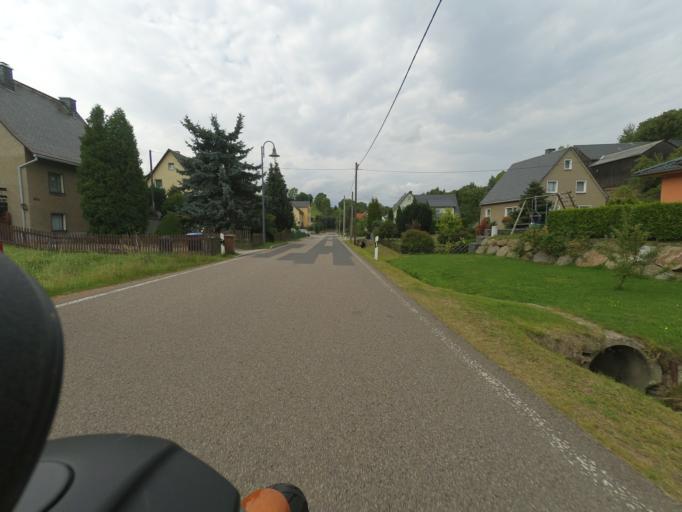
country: DE
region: Saxony
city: Glashutte
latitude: 50.8386
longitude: 13.8014
